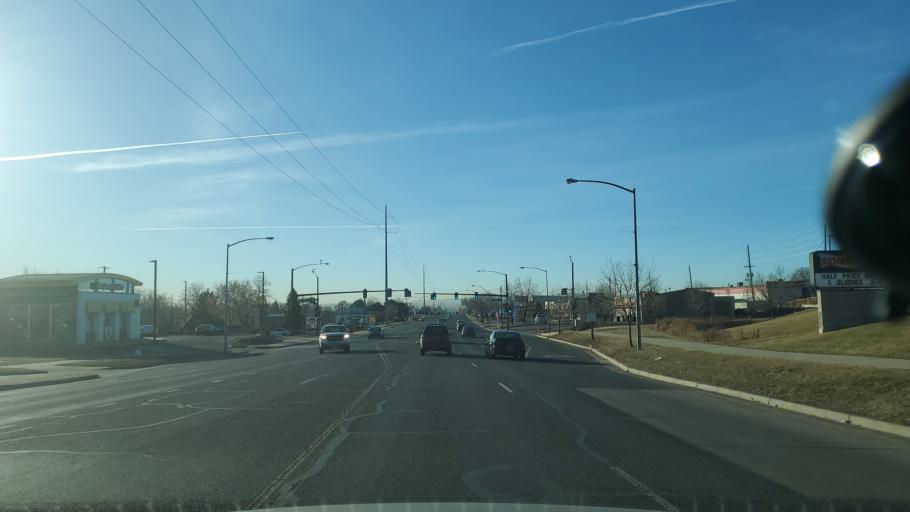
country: US
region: Colorado
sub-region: Adams County
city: Thornton
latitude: 39.8553
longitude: -104.9780
